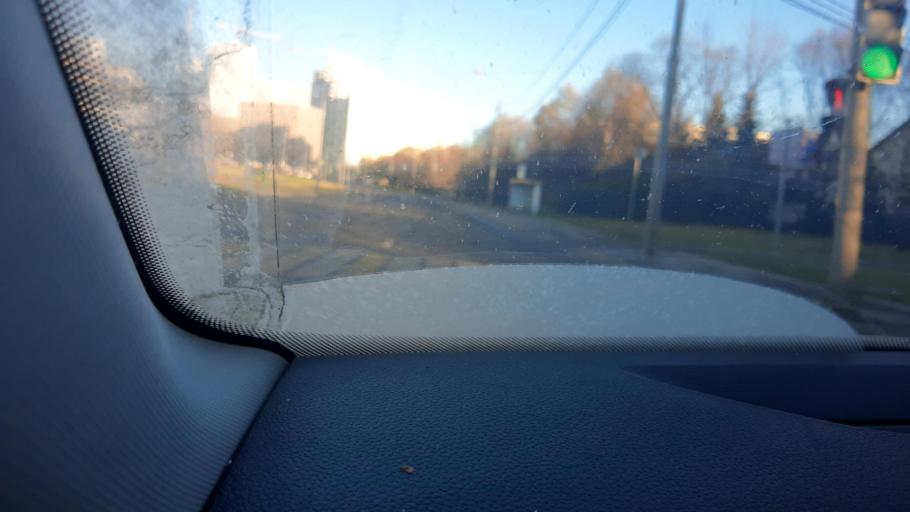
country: RU
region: Moskovskaya
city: Shcherbinka
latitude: 55.5501
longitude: 37.5461
